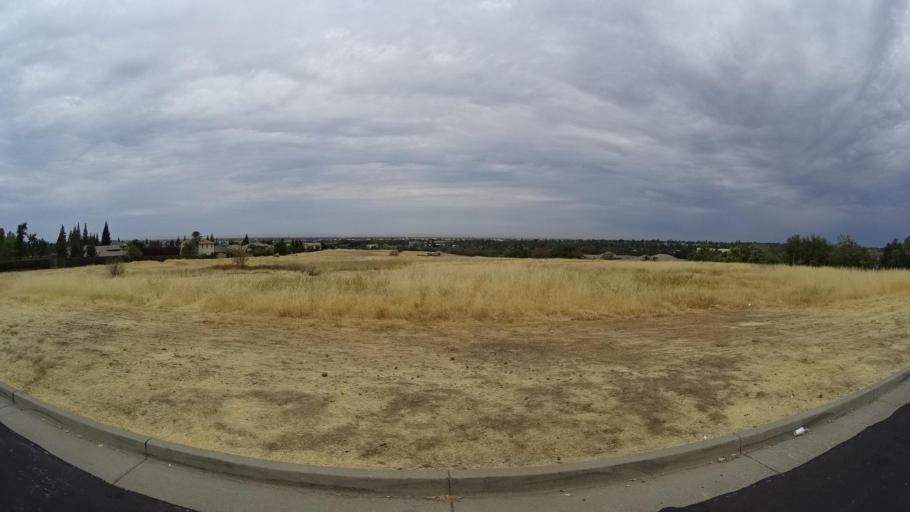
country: US
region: California
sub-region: Placer County
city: Rocklin
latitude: 38.7709
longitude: -121.2329
